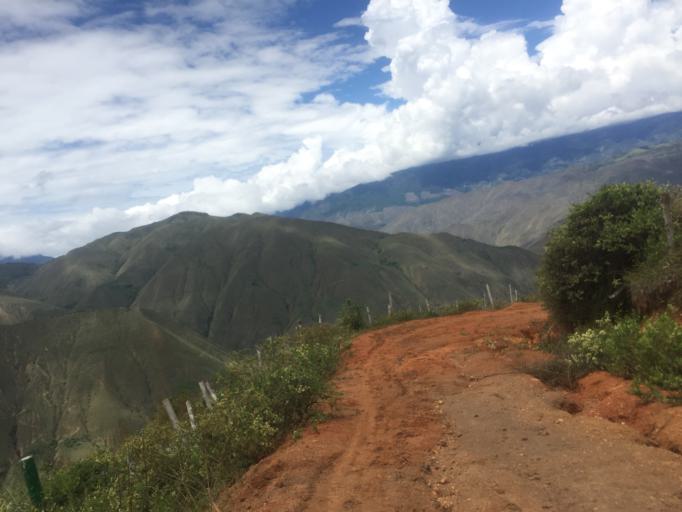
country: CO
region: Valle del Cauca
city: Dagua
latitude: 3.7144
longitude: -76.6044
